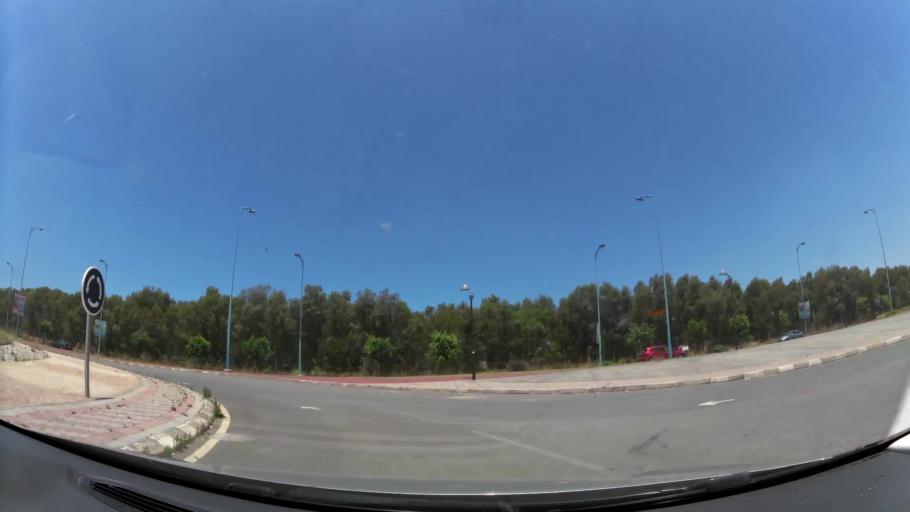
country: MA
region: Gharb-Chrarda-Beni Hssen
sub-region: Kenitra Province
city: Kenitra
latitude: 34.2718
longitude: -6.6282
